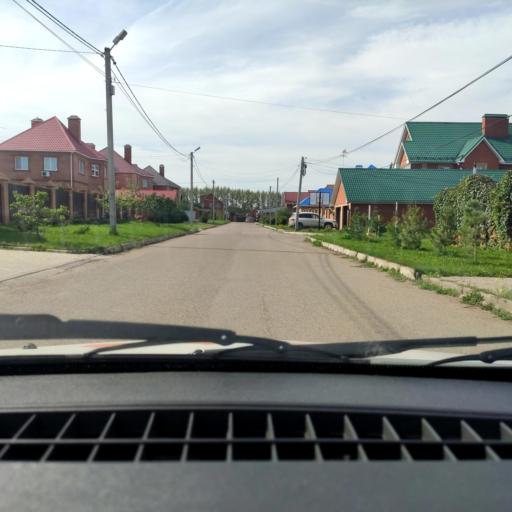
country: RU
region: Bashkortostan
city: Kabakovo
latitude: 54.6211
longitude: 56.1252
